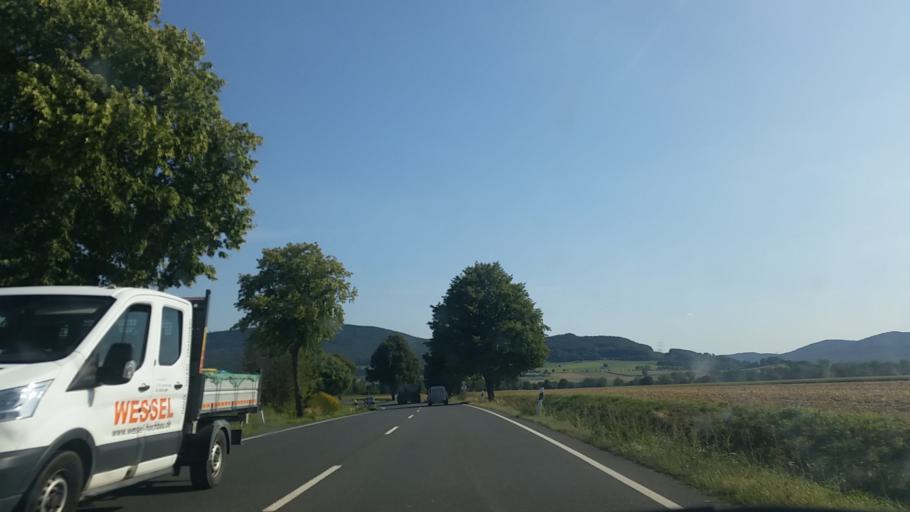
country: DE
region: Lower Saxony
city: Salzhemmendorf
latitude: 52.0894
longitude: 9.5950
